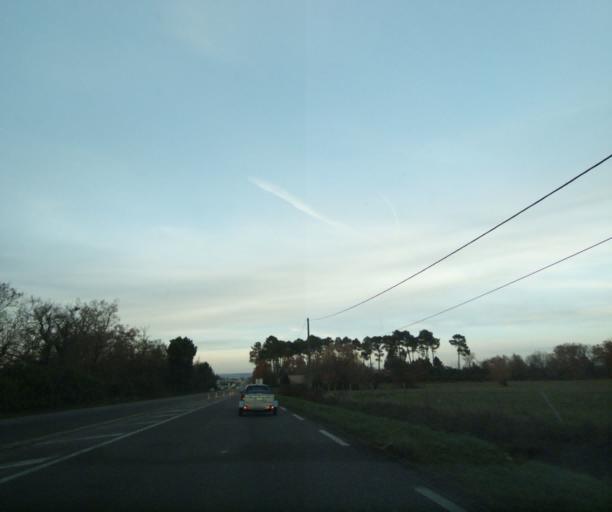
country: FR
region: Aquitaine
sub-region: Departement de la Gironde
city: Langon
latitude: 44.5129
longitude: -0.2391
